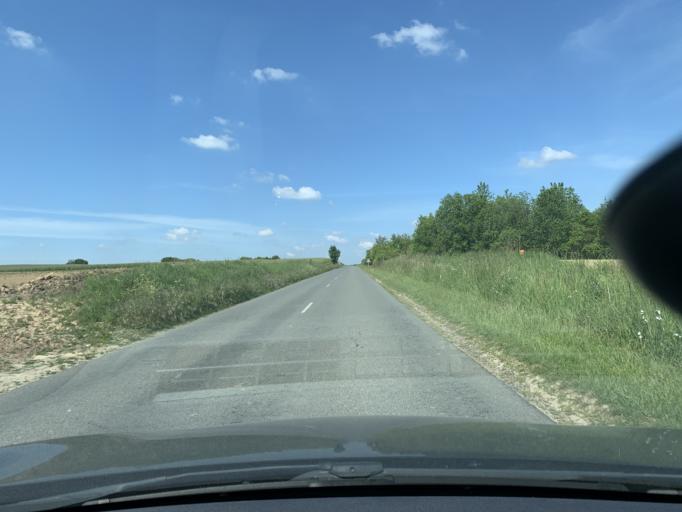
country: FR
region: Nord-Pas-de-Calais
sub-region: Departement du Nord
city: Aubigny-au-Bac
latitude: 50.2595
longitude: 3.1469
